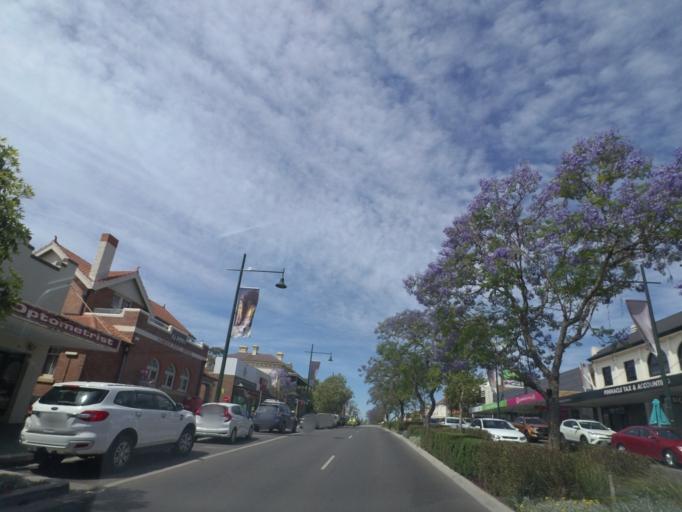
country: AU
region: New South Wales
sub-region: Camden
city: Elderslie
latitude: -34.0550
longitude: 150.6947
